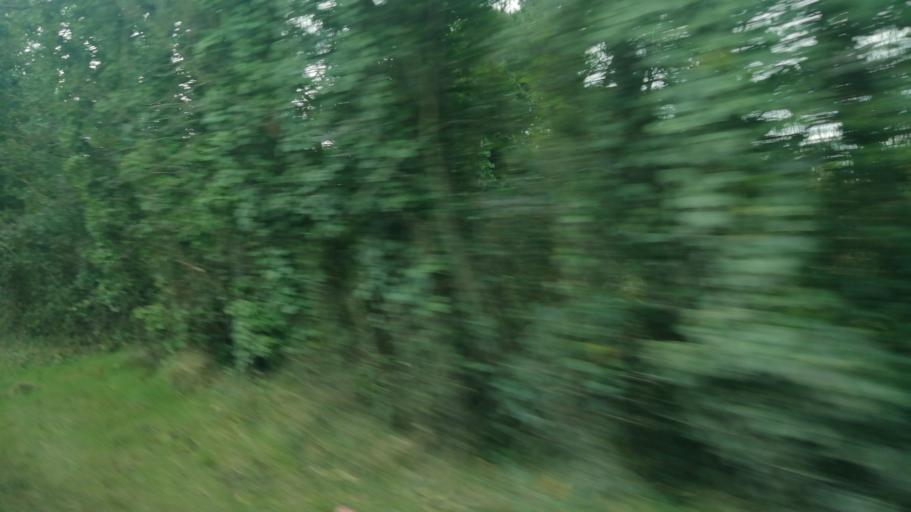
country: IE
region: Leinster
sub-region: Kildare
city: Derrinturn
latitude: 53.2881
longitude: -6.8952
